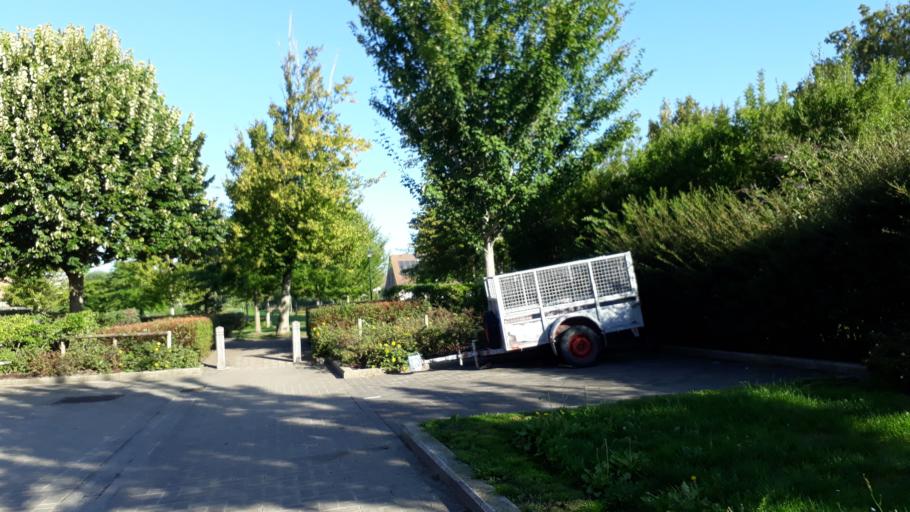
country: BE
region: Flanders
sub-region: Provincie West-Vlaanderen
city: Torhout
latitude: 51.0661
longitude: 3.1162
